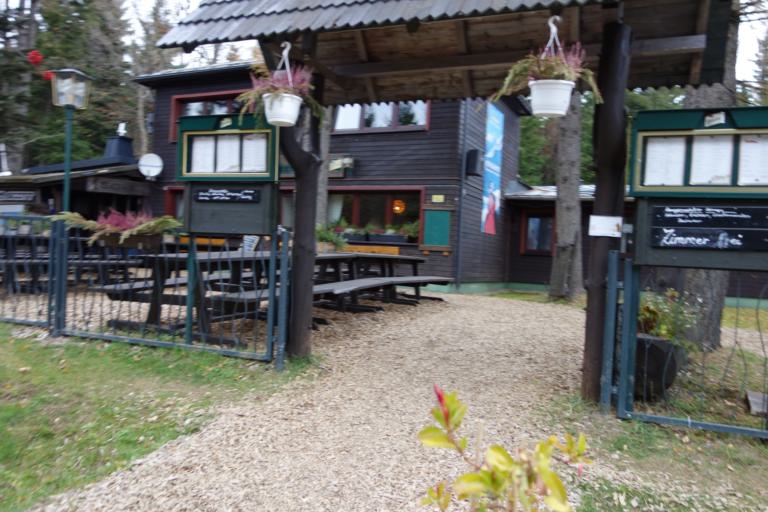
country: DE
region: Saxony
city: Kurort Oberwiesenthal
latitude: 50.4361
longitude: 12.9674
